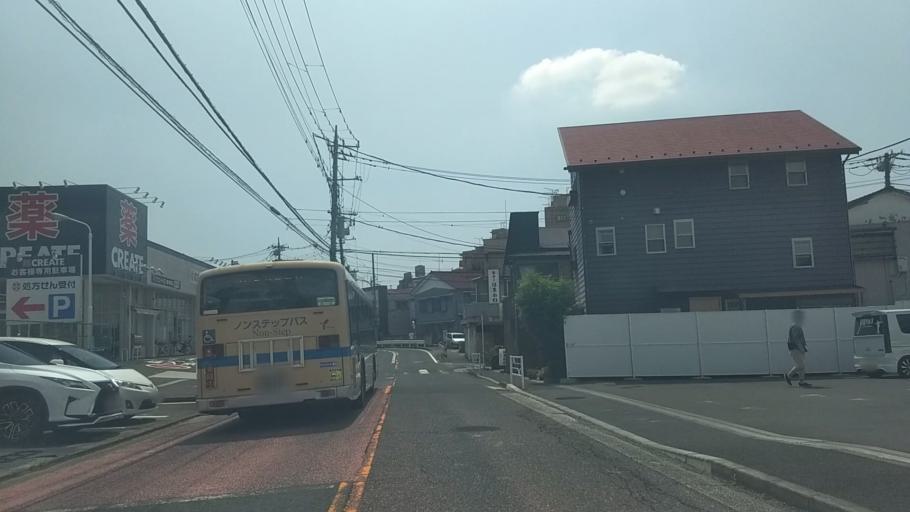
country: JP
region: Kanagawa
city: Yokohama
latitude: 35.5016
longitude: 139.6545
